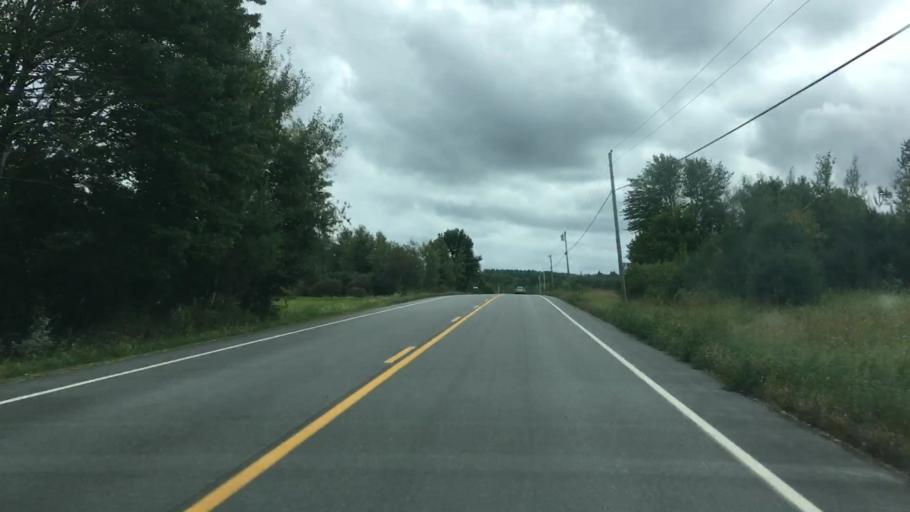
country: US
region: Maine
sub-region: Penobscot County
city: Hermon
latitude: 44.7495
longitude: -68.9693
